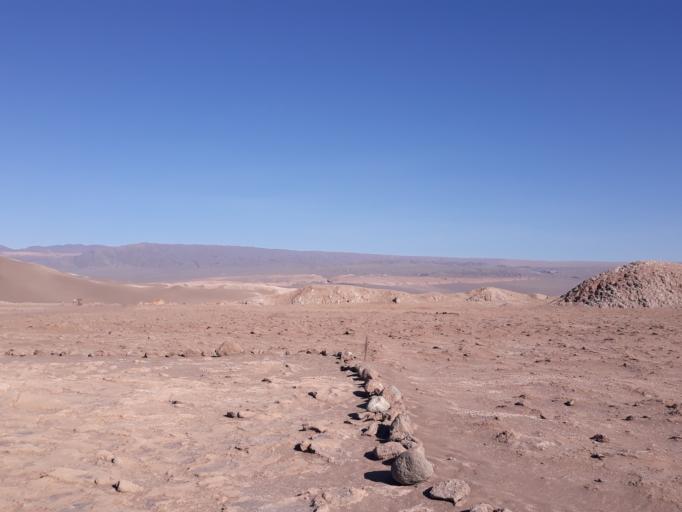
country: CL
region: Antofagasta
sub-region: Provincia de El Loa
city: San Pedro de Atacama
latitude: -22.9197
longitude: -68.3192
